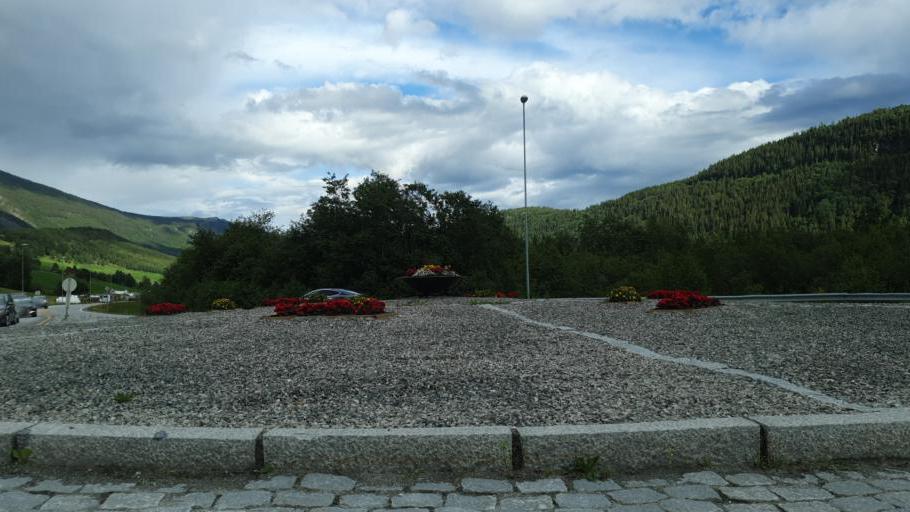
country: NO
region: Oppland
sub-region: Vaga
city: Vagamo
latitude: 61.8765
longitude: 9.1286
